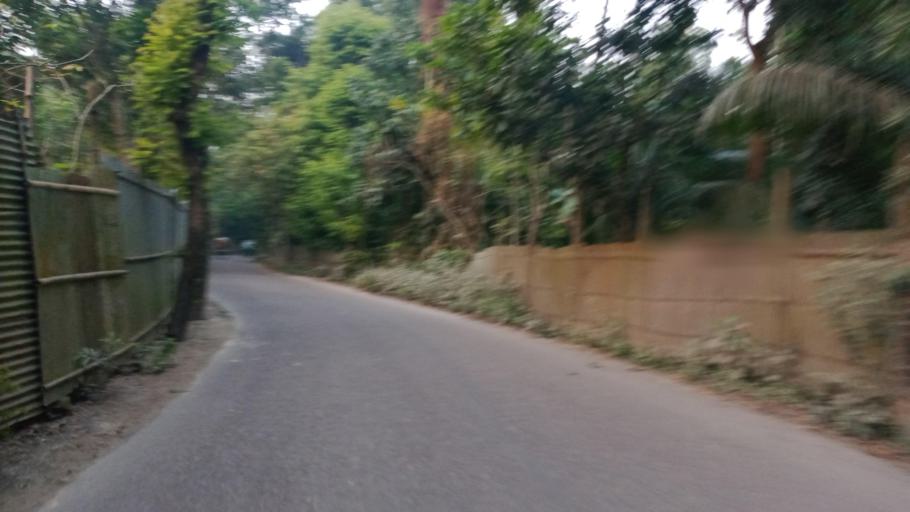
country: BD
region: Chittagong
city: Hajiganj
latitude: 23.3742
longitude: 90.9837
